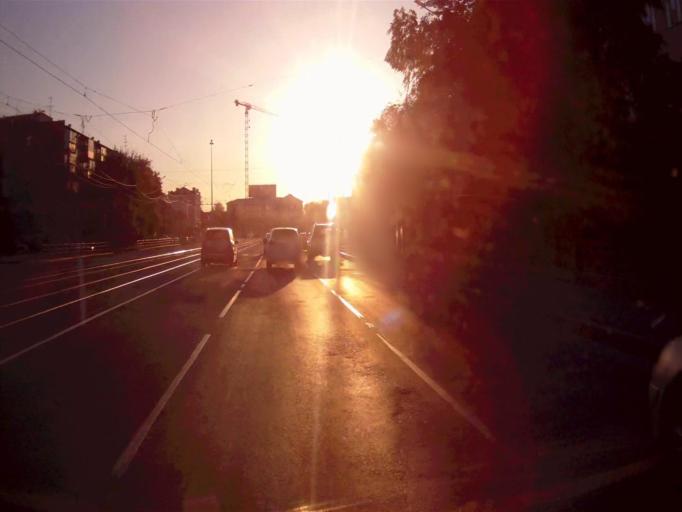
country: RU
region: Chelyabinsk
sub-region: Gorod Chelyabinsk
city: Chelyabinsk
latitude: 55.1680
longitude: 61.4188
